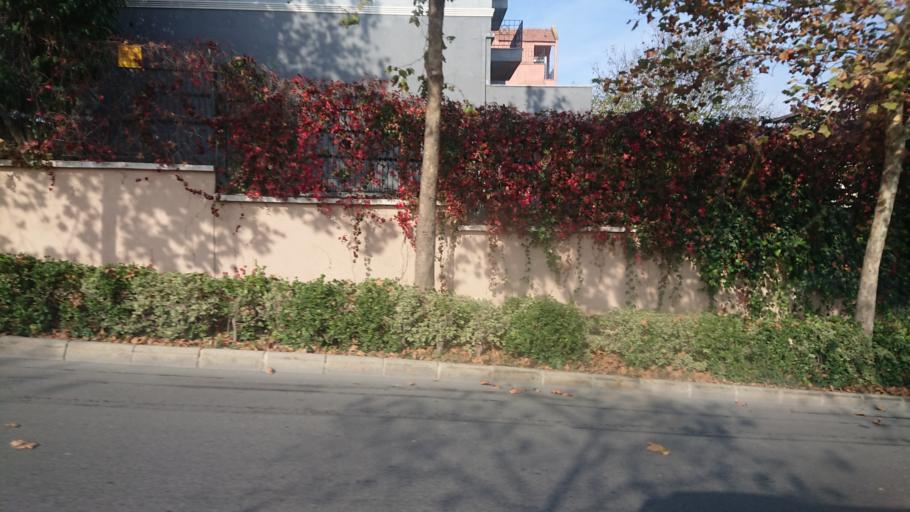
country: TR
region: Istanbul
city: Esenyurt
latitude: 41.0782
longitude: 28.6743
